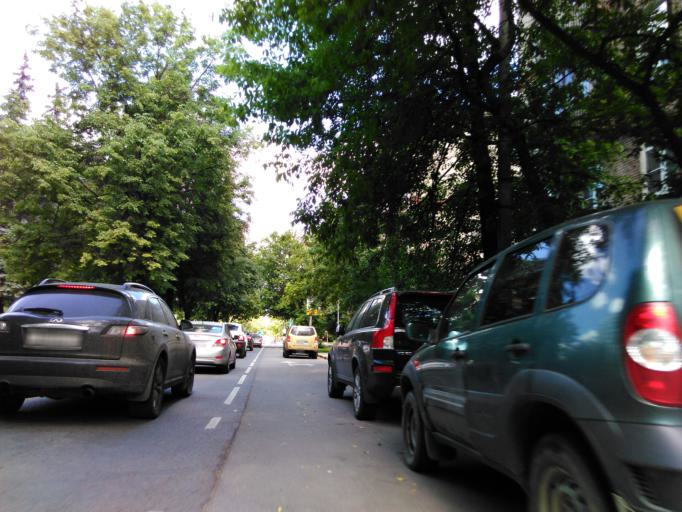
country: RU
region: Moscow
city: Novyye Cheremushki
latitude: 55.6876
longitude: 37.5857
